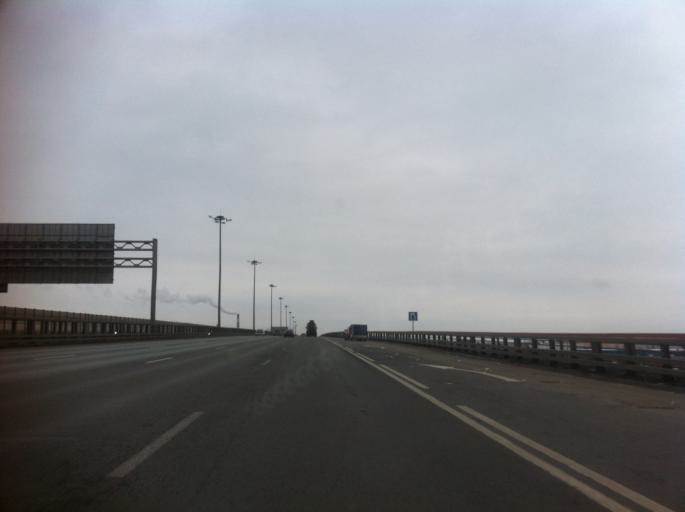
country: RU
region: St.-Petersburg
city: Shushary
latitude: 59.8165
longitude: 30.3865
